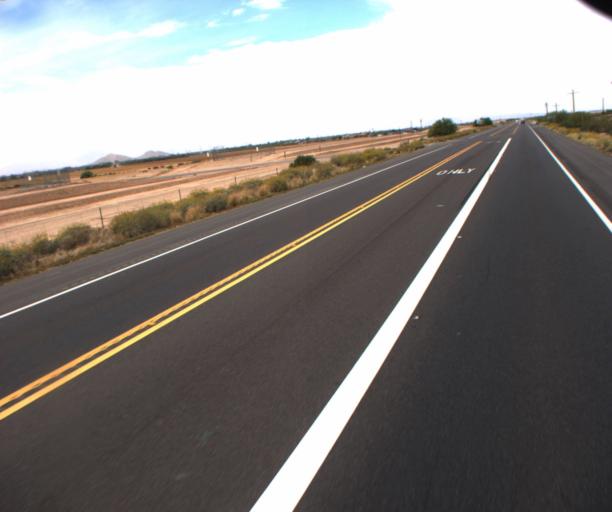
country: US
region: Arizona
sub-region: Pinal County
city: Sacaton
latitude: 33.1443
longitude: -111.7624
